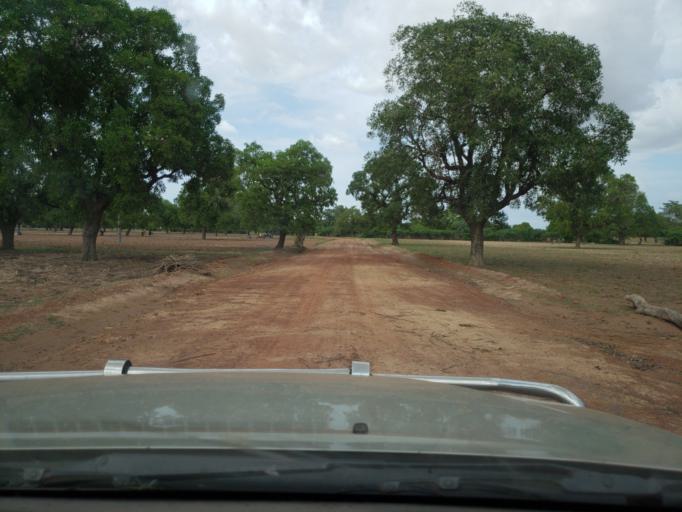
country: ML
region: Segou
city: Bla
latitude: 12.7209
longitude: -5.6784
